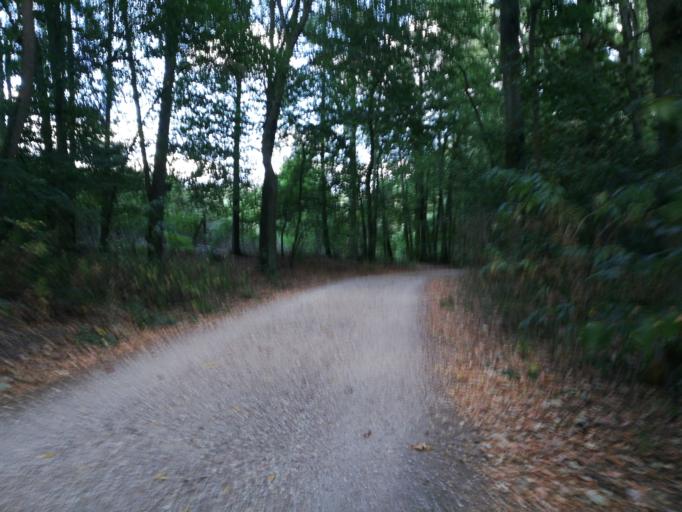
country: DE
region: Bavaria
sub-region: Regierungsbezirk Mittelfranken
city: Zirndorf
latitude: 49.4692
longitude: 10.9244
